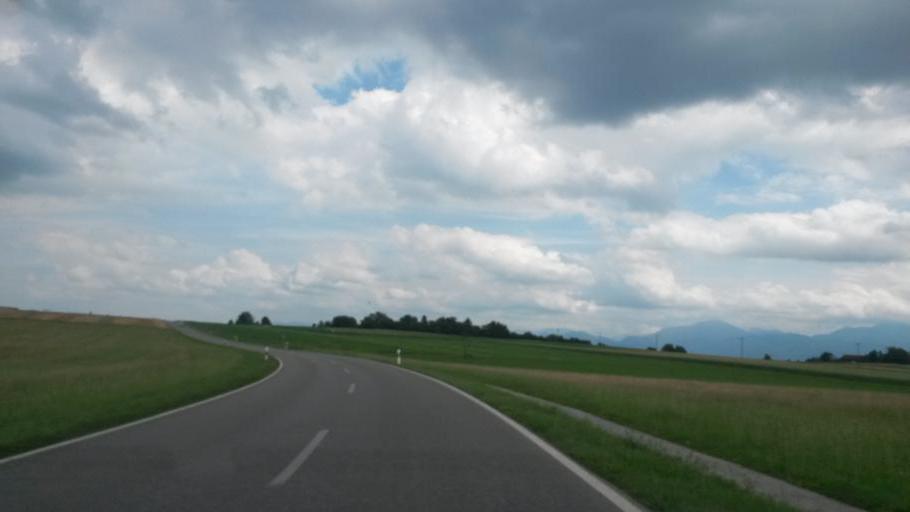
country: DE
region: Bavaria
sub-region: Upper Bavaria
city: Gstadt am Chiemsee
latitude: 47.8875
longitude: 12.4034
